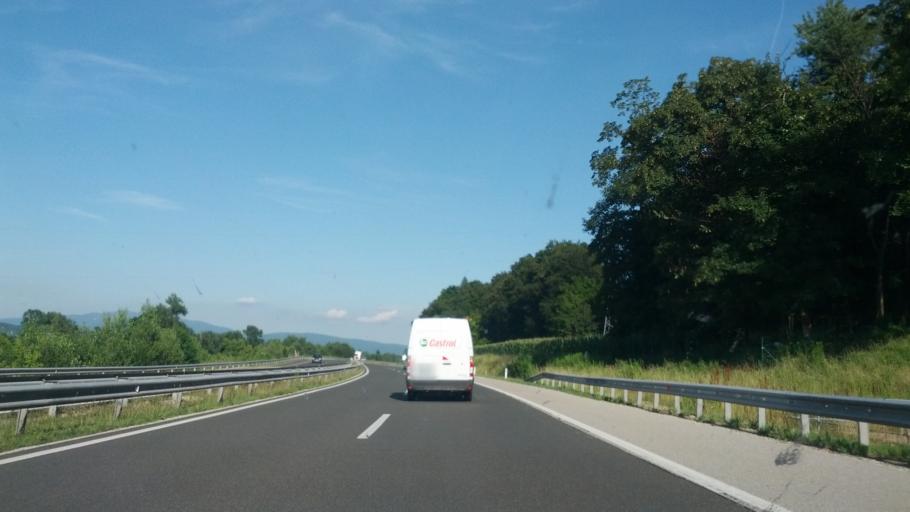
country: SI
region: Brezice
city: Brezice
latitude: 45.8763
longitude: 15.6418
